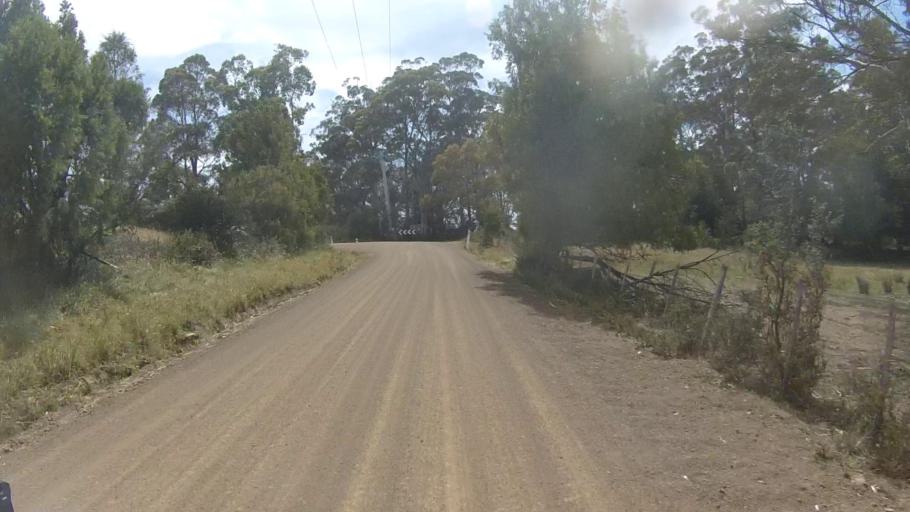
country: AU
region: Tasmania
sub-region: Sorell
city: Sorell
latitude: -42.7918
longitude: 147.8462
